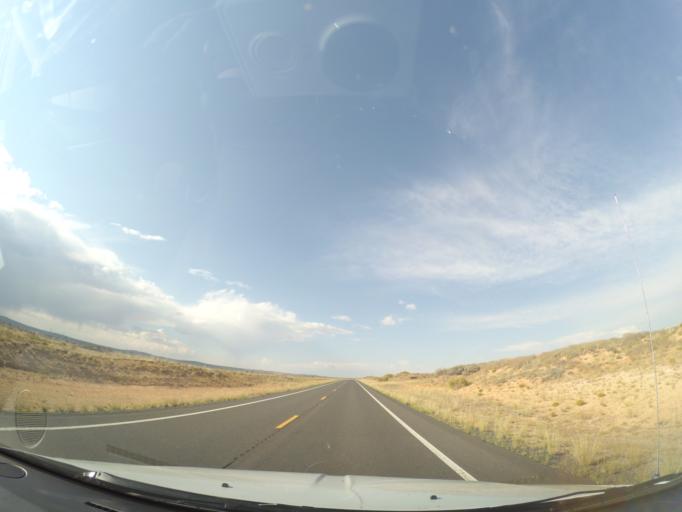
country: US
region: Arizona
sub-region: Coconino County
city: Tuba City
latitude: 36.4392
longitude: -111.4240
